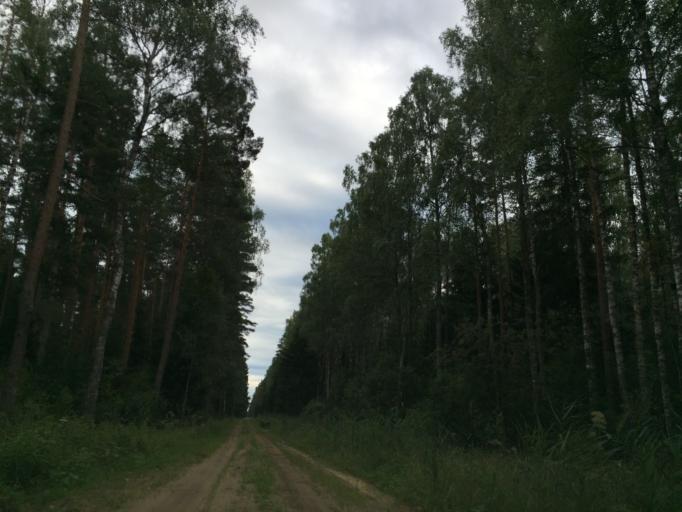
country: LV
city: Tireli
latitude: 56.8514
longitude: 23.6827
